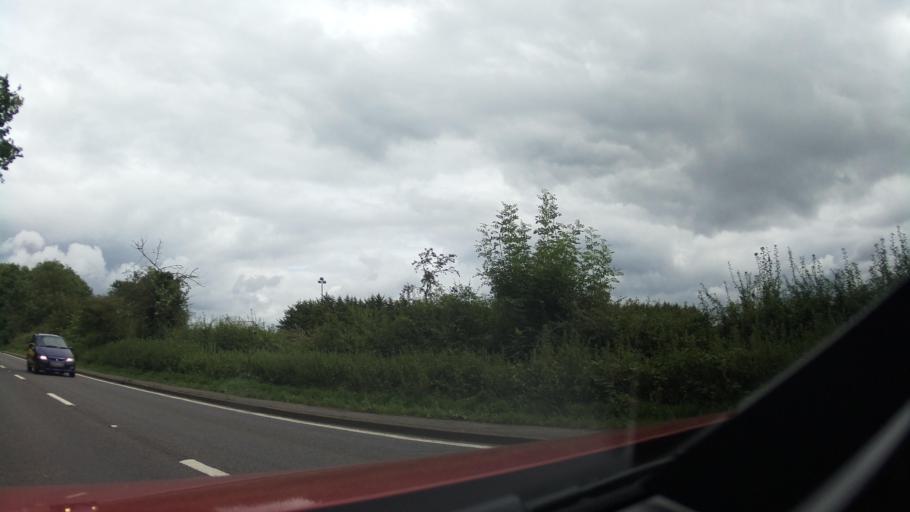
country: GB
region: England
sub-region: Northamptonshire
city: Corby
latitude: 52.5056
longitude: -0.7214
